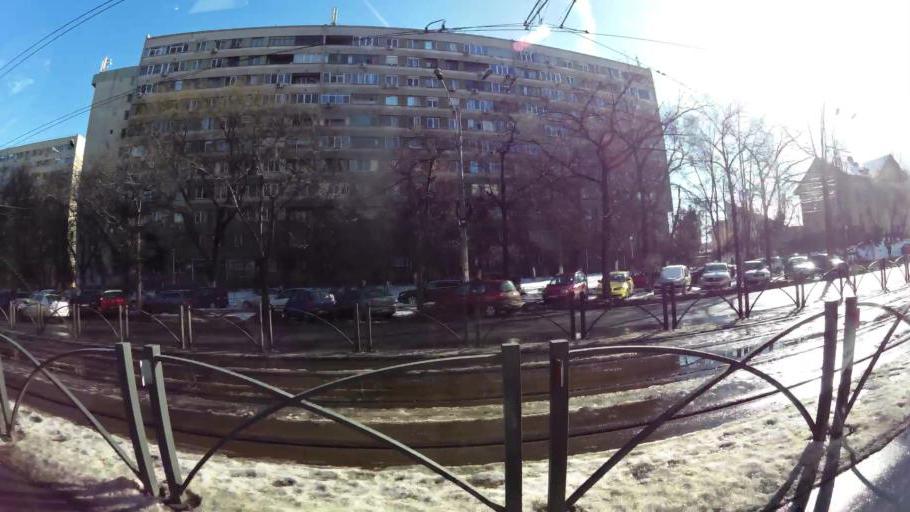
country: RO
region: Bucuresti
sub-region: Municipiul Bucuresti
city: Bucharest
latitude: 44.4555
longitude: 26.1291
